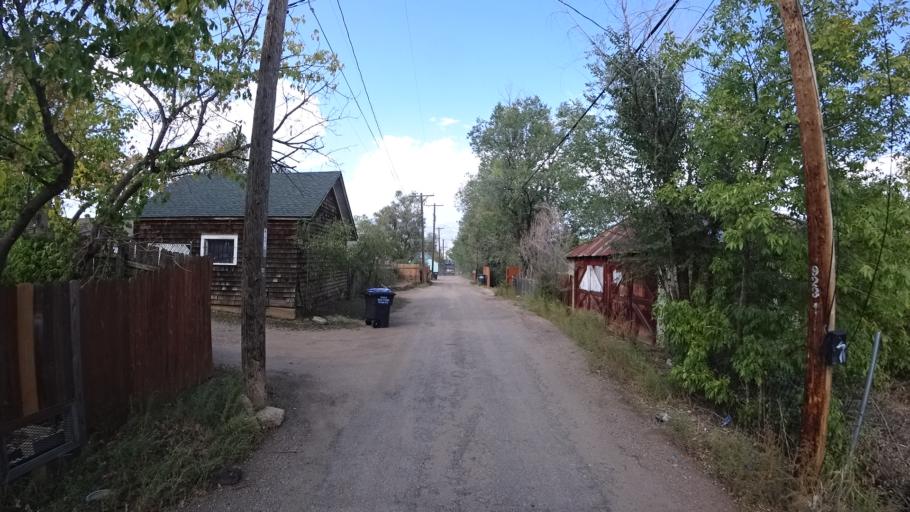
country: US
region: Colorado
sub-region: El Paso County
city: Colorado Springs
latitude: 38.8284
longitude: -104.8069
